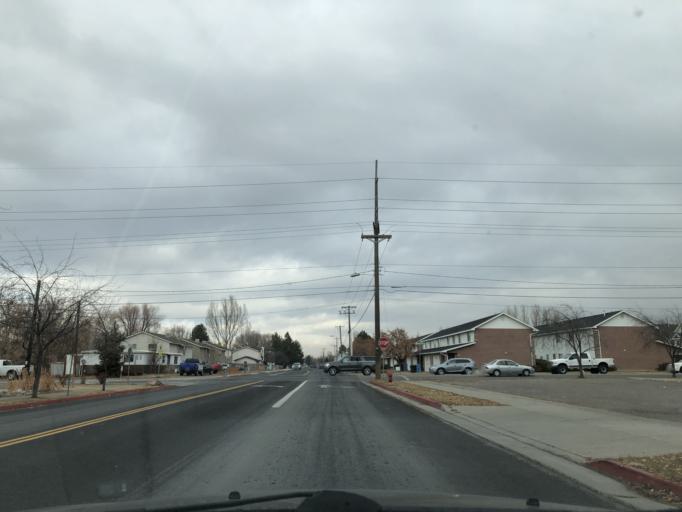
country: US
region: Utah
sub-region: Cache County
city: Logan
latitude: 41.7497
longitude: -111.8394
